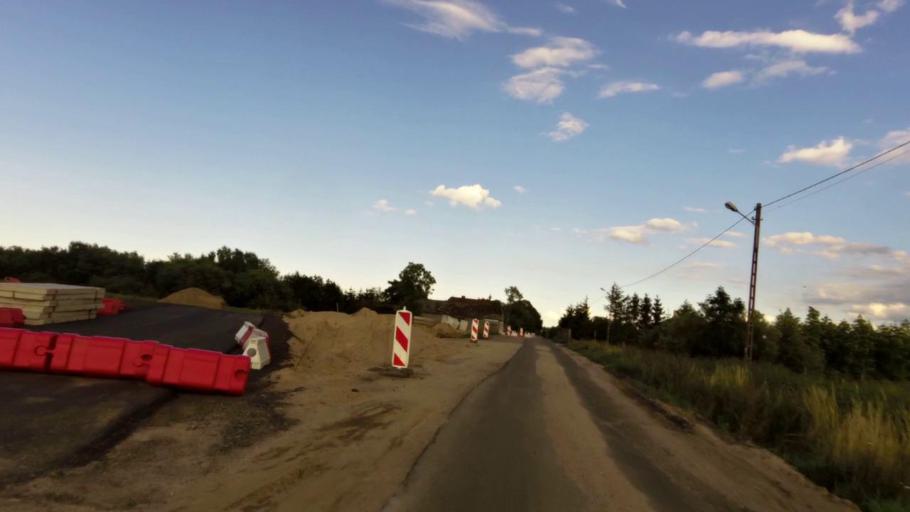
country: PL
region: West Pomeranian Voivodeship
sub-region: Powiat slawienski
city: Darlowo
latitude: 54.4044
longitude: 16.3768
